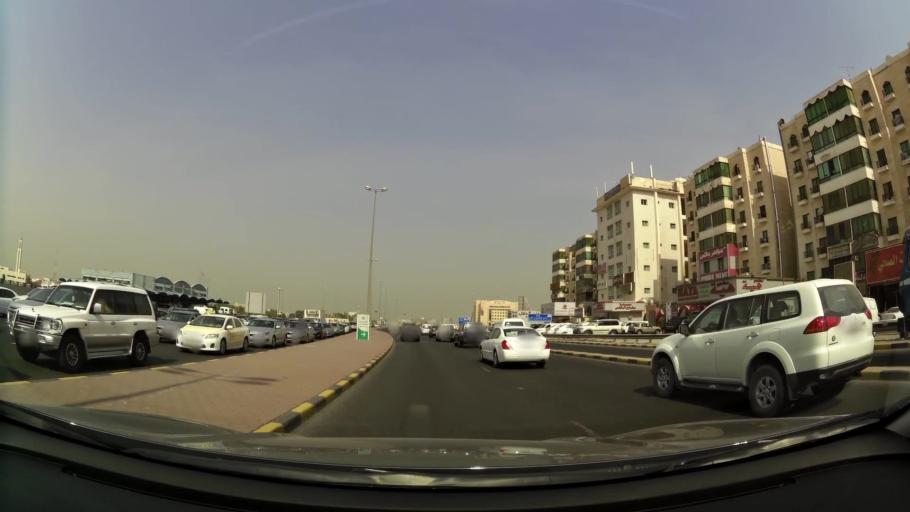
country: KW
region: Al Asimah
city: Ar Rabiyah
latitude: 29.3000
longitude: 47.9058
